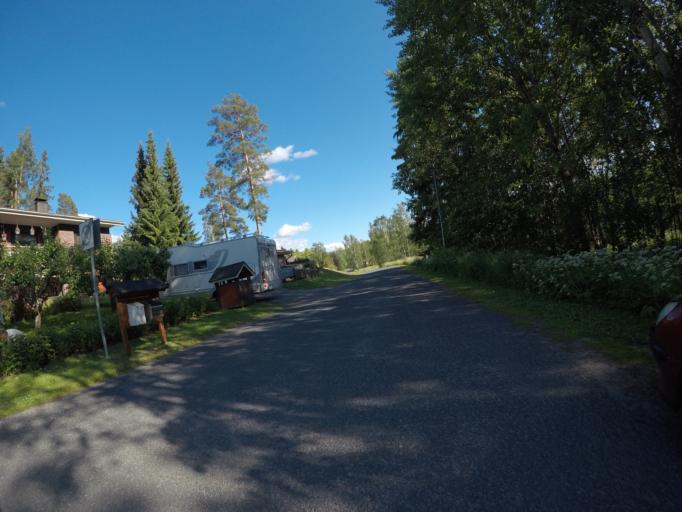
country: FI
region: Haeme
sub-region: Haemeenlinna
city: Haemeenlinna
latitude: 61.0198
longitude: 24.4966
